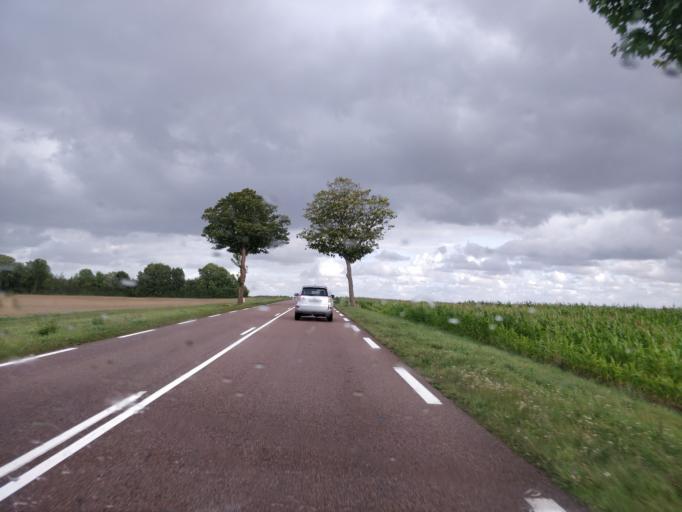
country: FR
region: Champagne-Ardenne
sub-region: Departement de l'Aube
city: Verrieres
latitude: 48.2834
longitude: 4.1731
